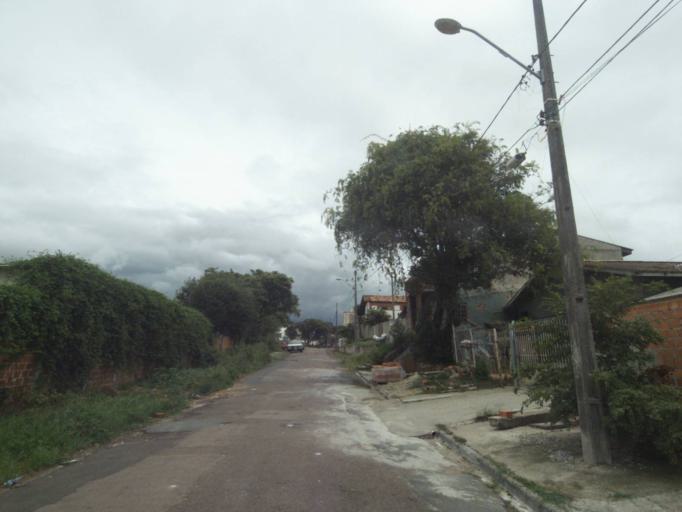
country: BR
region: Parana
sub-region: Curitiba
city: Curitiba
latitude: -25.4865
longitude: -49.2882
